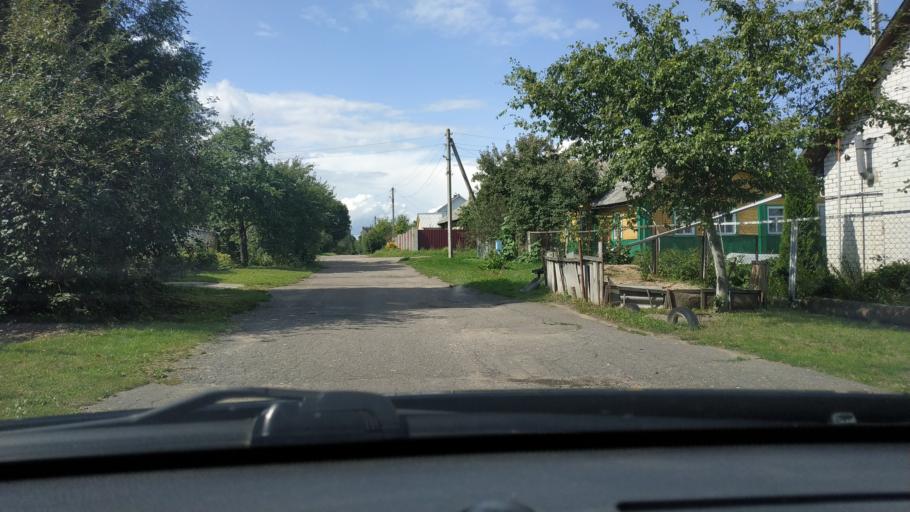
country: BY
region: Mogilev
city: Mahilyow
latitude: 53.9026
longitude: 30.2919
